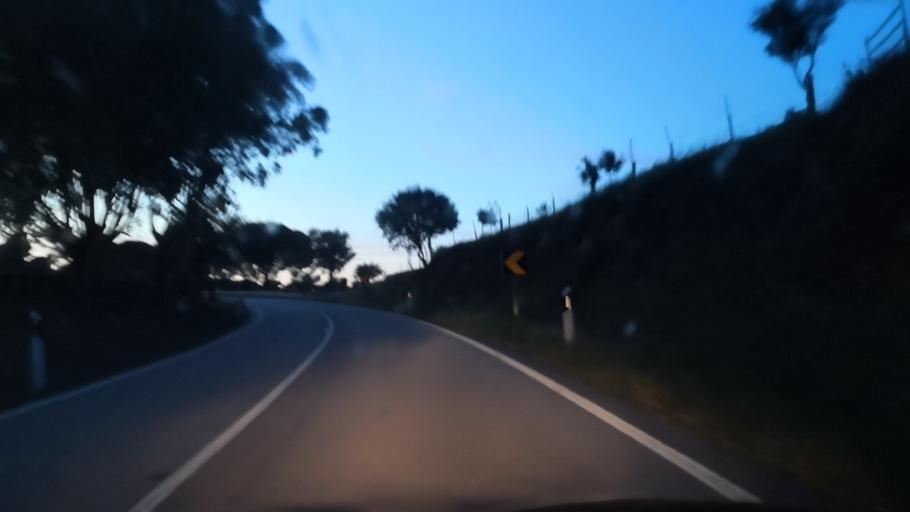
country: ES
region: Extremadura
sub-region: Provincia de Caceres
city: Piedras Albas
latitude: 39.8402
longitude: -6.9748
